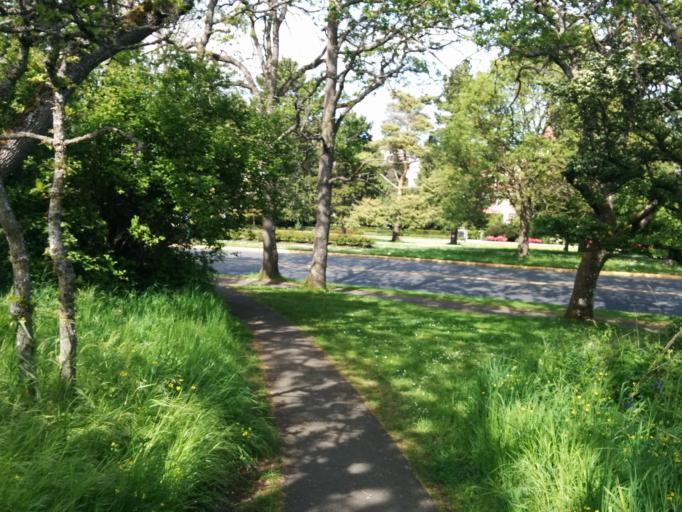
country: CA
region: British Columbia
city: Victoria
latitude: 48.4180
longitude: -123.3647
